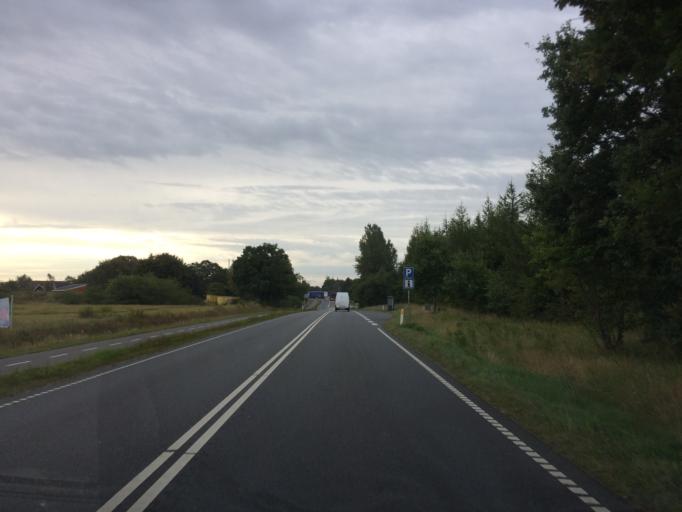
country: DK
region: Central Jutland
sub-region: Ikast-Brande Kommune
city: Brande
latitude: 55.9591
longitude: 9.1051
